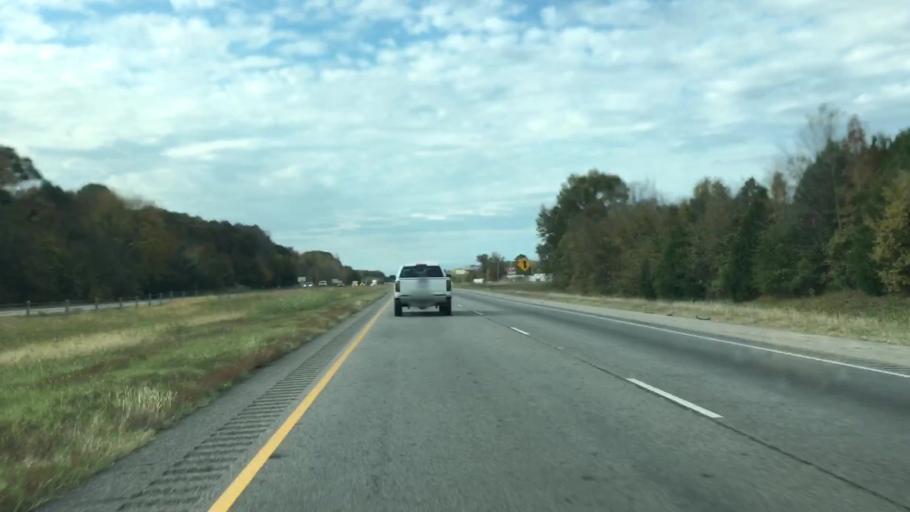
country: US
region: Arkansas
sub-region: Pope County
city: Atkins
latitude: 35.2198
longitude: -92.8305
